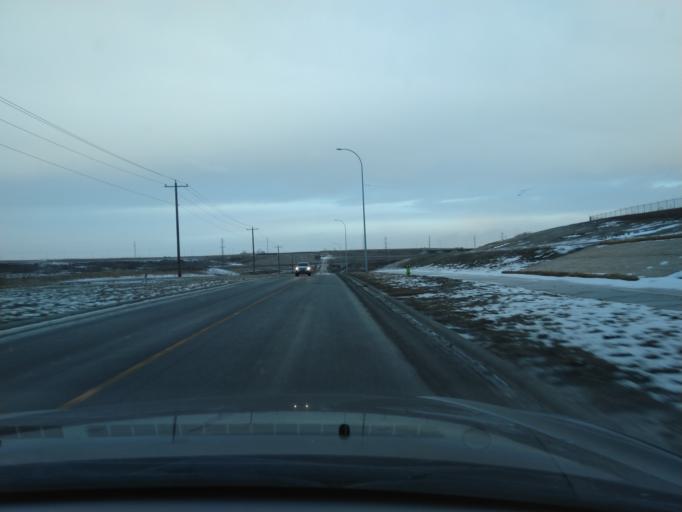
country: CA
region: Alberta
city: Calgary
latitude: 51.1659
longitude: -114.0247
